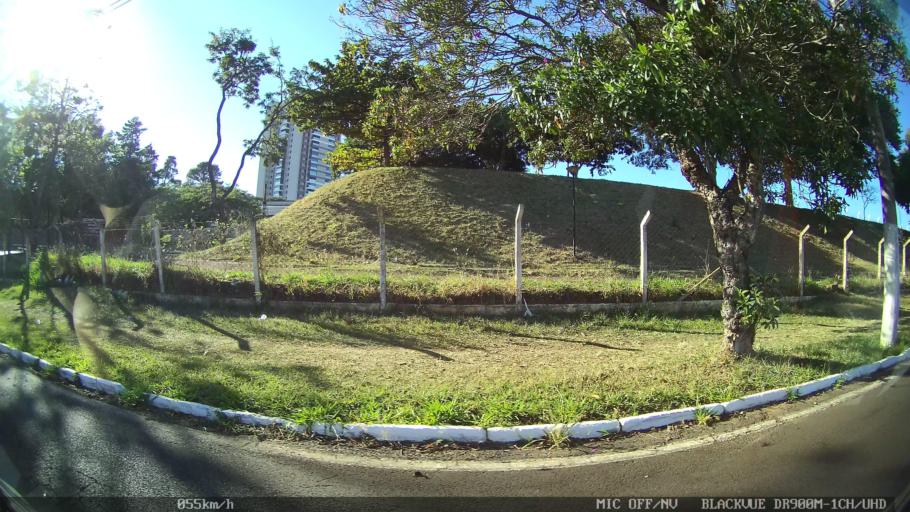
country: BR
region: Sao Paulo
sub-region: Franca
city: Franca
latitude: -20.5589
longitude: -47.4087
